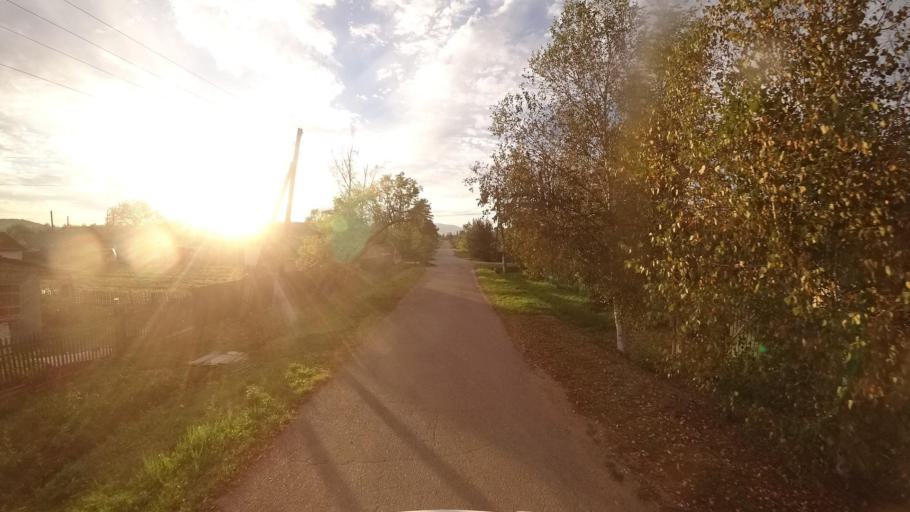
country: RU
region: Primorskiy
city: Yakovlevka
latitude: 44.4254
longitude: 133.4847
